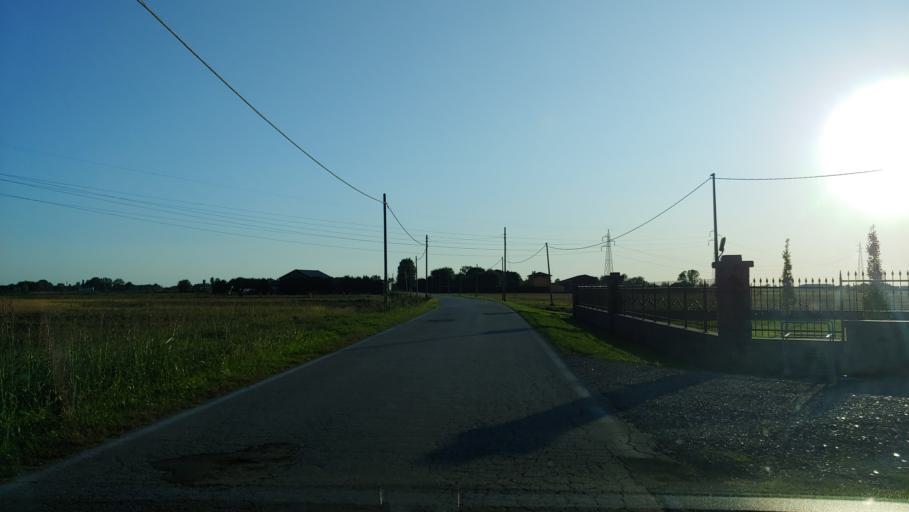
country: IT
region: Veneto
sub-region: Provincia di Rovigo
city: Pettorazza Grimani
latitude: 45.0745
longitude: 11.9958
